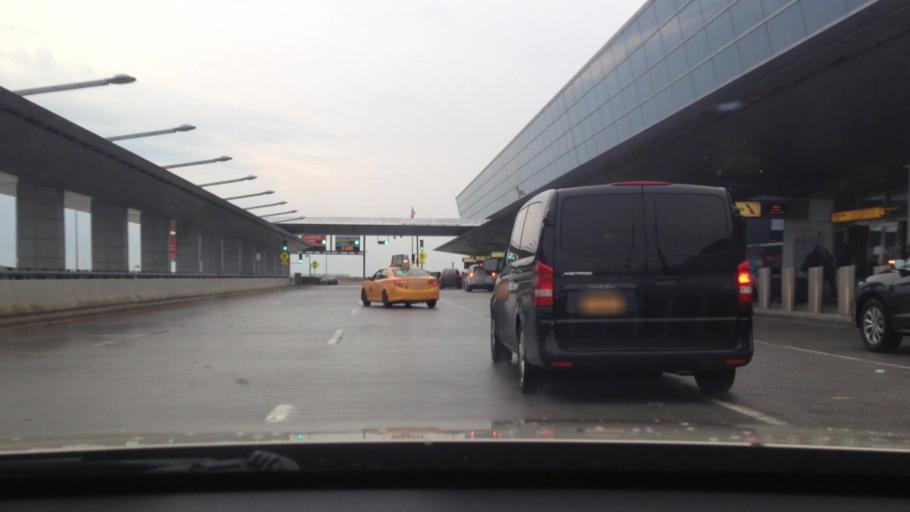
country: US
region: New York
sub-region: Queens County
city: Jamaica
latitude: 40.6471
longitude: -73.7894
